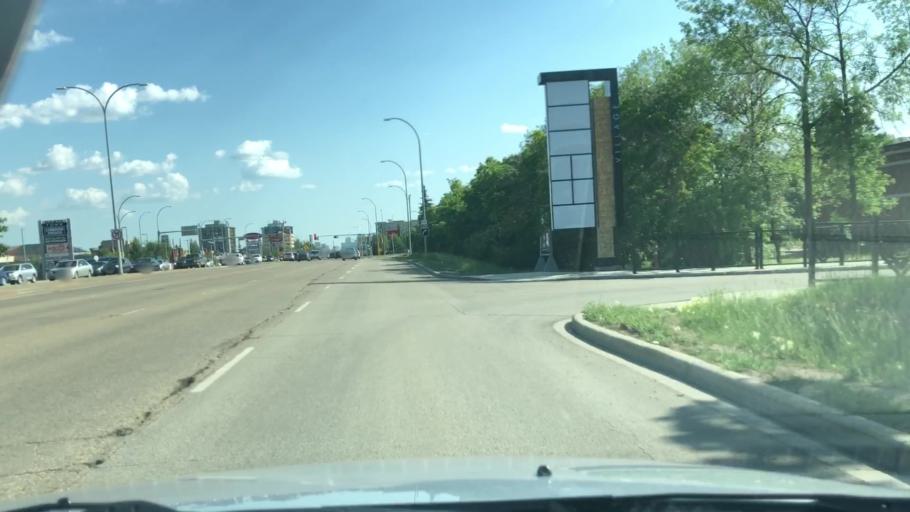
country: CA
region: Alberta
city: Edmonton
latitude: 53.6014
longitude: -113.4922
